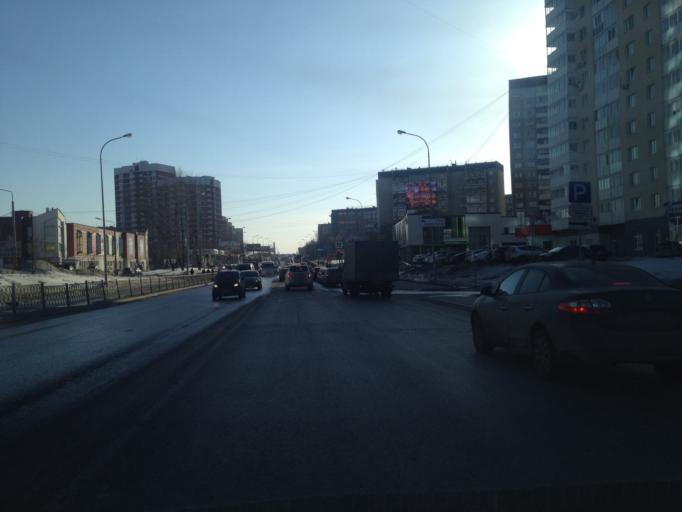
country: RU
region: Sverdlovsk
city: Yekaterinburg
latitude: 56.8543
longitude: 60.5732
